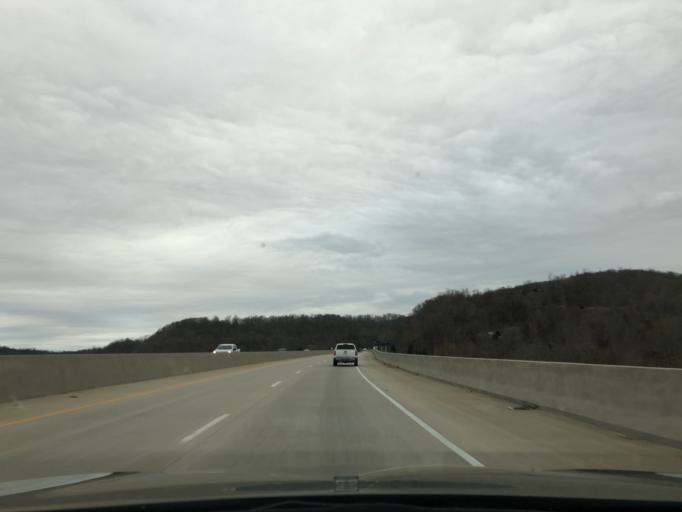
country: US
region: Arkansas
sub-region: Washington County
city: West Fork
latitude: 35.7804
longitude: -94.1864
